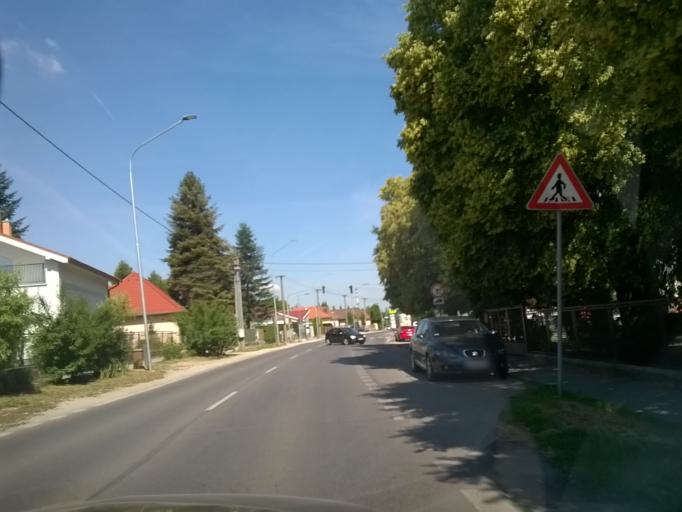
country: SK
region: Nitriansky
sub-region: Okres Nitra
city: Nitra
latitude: 48.3129
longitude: 18.0556
